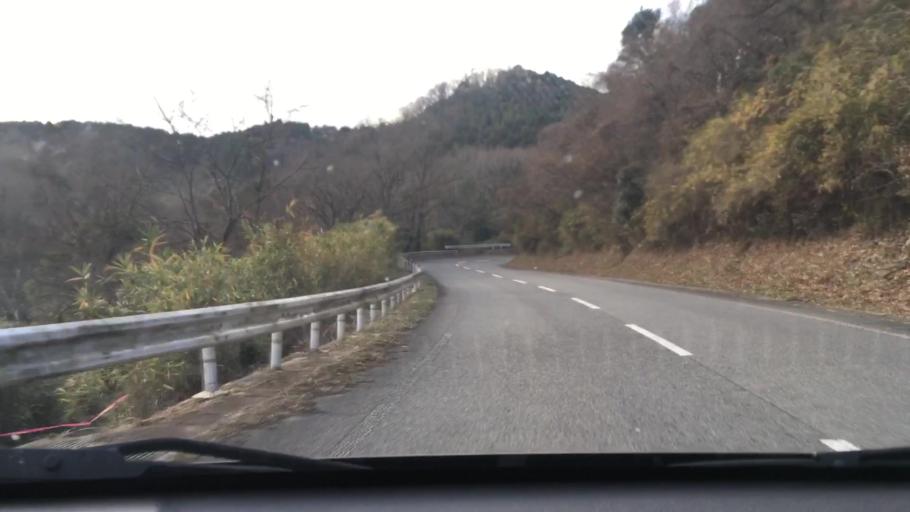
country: JP
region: Oita
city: Hiji
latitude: 33.4138
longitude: 131.4216
